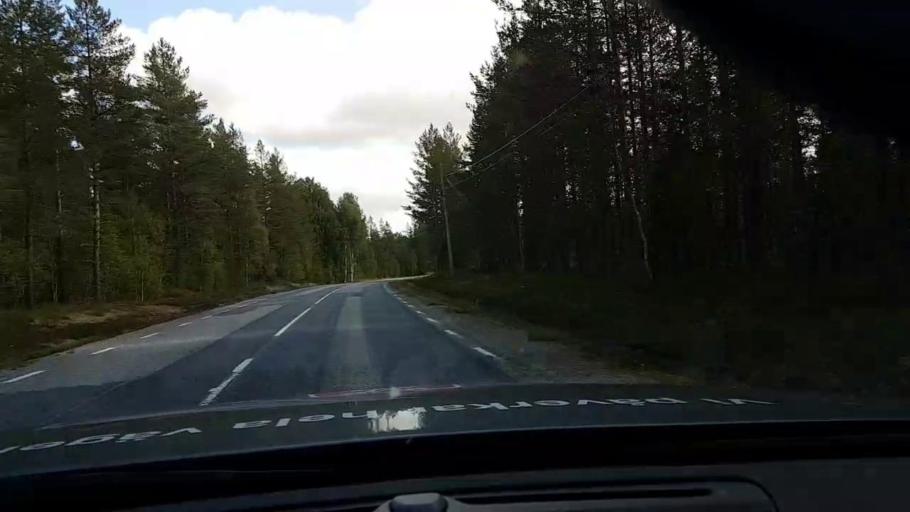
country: SE
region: Vaesterbotten
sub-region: Asele Kommun
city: Asele
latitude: 63.7921
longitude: 17.5812
